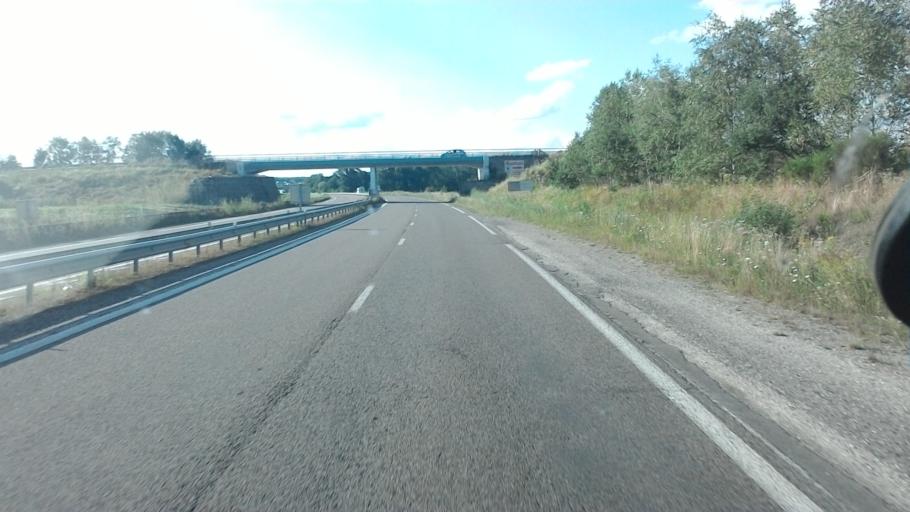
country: FR
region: Franche-Comte
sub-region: Departement de la Haute-Saone
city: Froideconche
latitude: 47.8085
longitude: 6.4038
